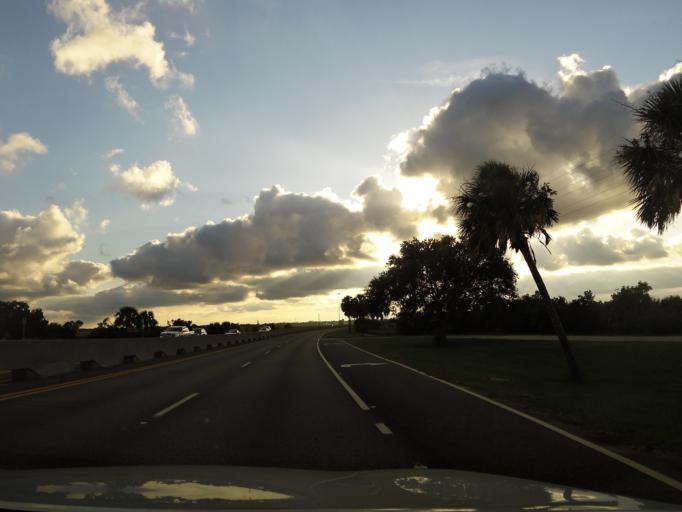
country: US
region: Georgia
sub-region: Glynn County
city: Saint Simon Mills
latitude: 31.1634
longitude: -81.4496
